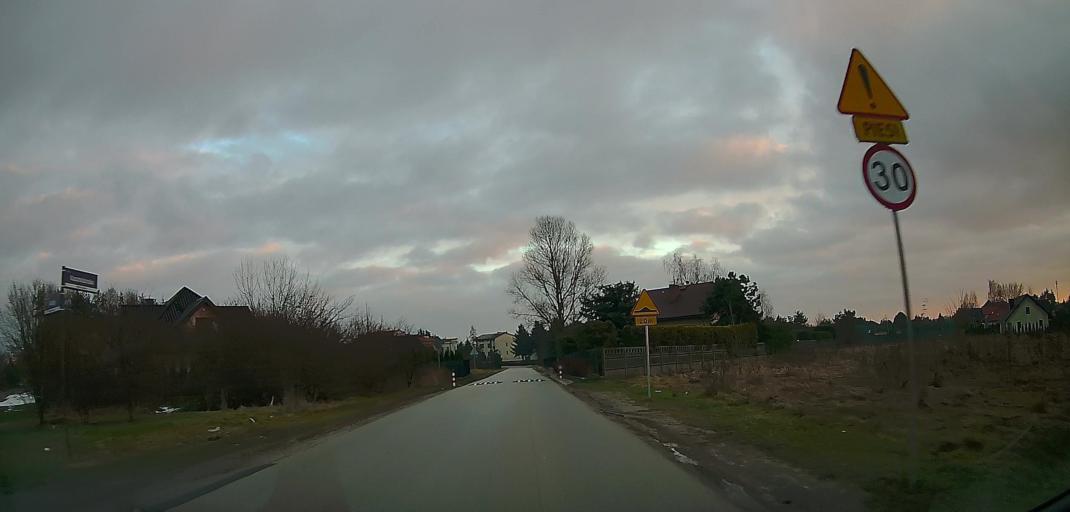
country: PL
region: Masovian Voivodeship
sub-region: Radom
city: Radom
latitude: 51.4484
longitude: 21.1390
